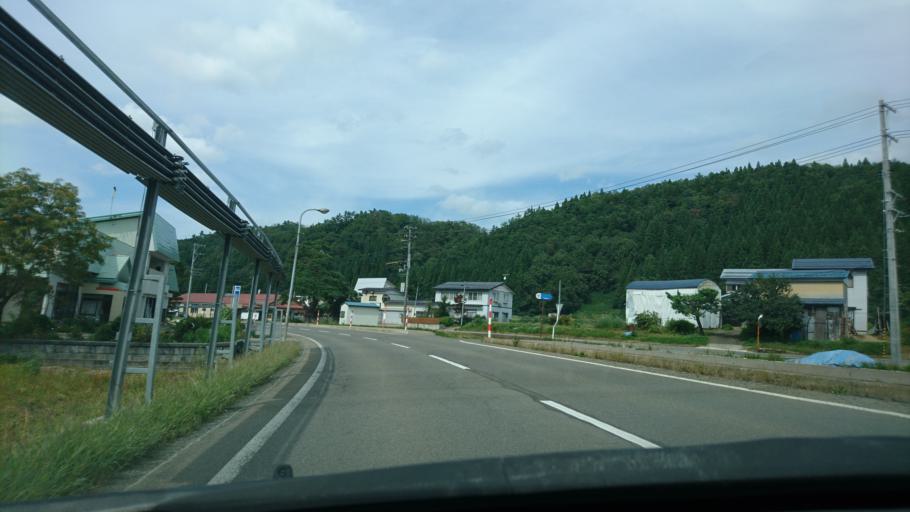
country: JP
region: Akita
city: Yuzawa
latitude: 39.1925
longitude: 140.6184
